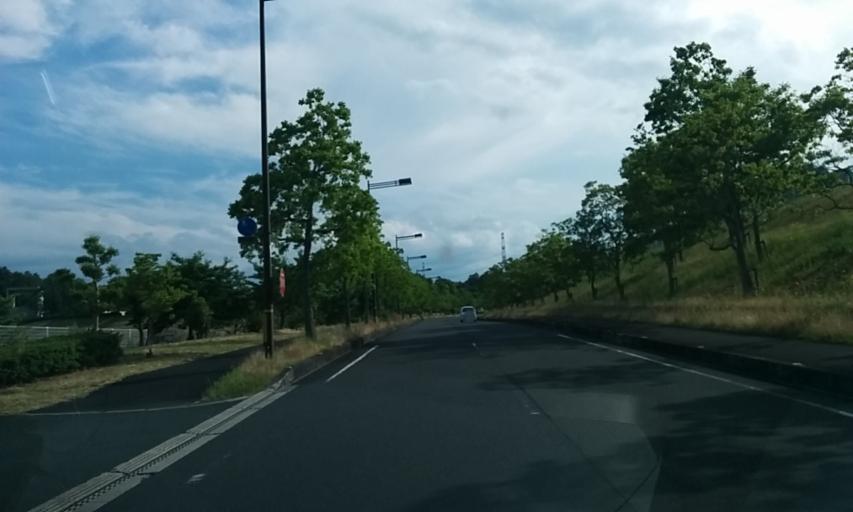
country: JP
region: Kyoto
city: Ayabe
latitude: 35.3322
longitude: 135.2884
